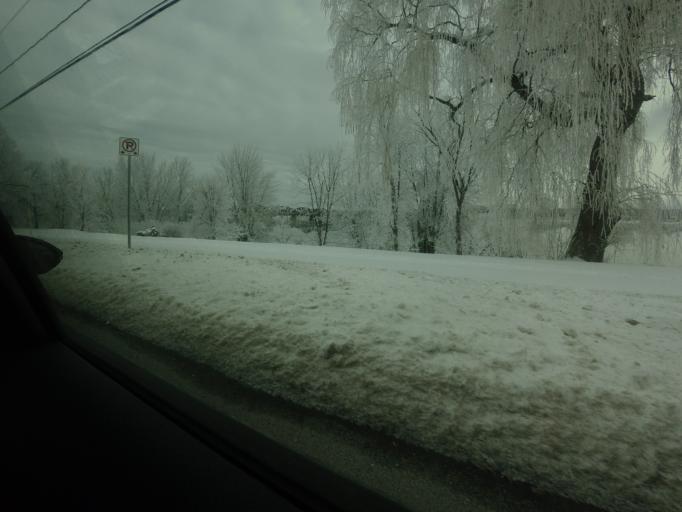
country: CA
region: New Brunswick
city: Fredericton
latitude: 45.9544
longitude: -66.6326
